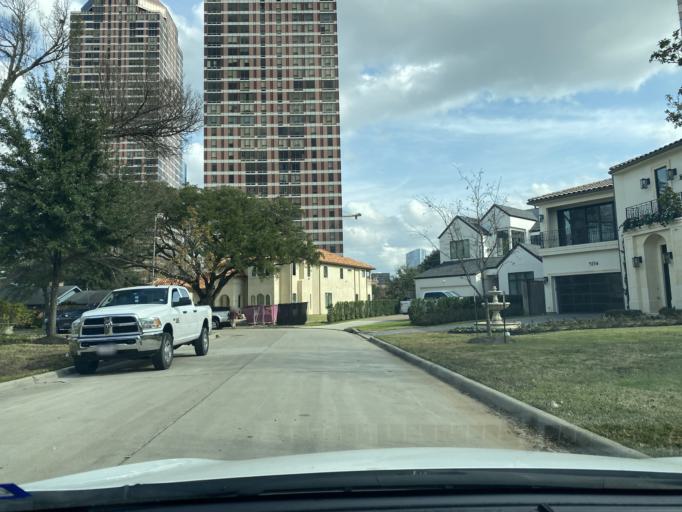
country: US
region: Texas
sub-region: Harris County
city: Hunters Creek Village
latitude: 29.7508
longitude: -95.4661
